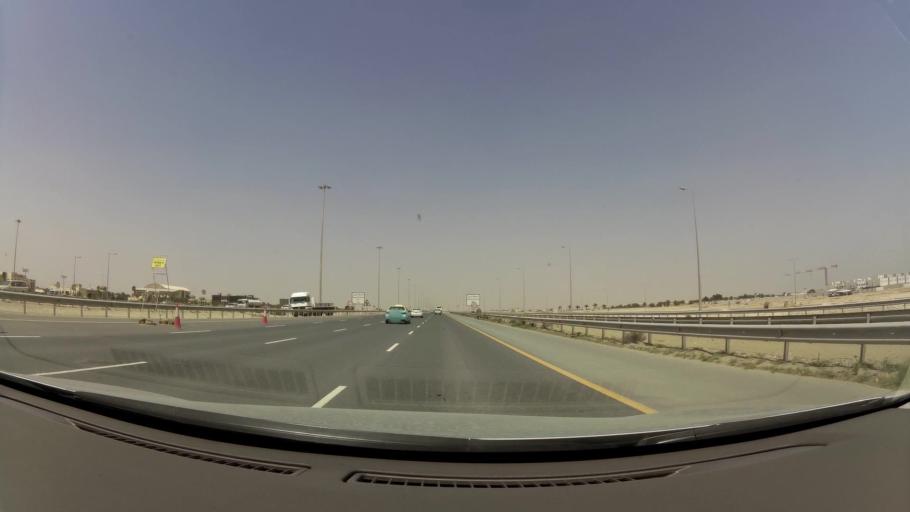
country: QA
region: Baladiyat Umm Salal
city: Umm Salal `Ali
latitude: 25.4539
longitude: 51.4097
